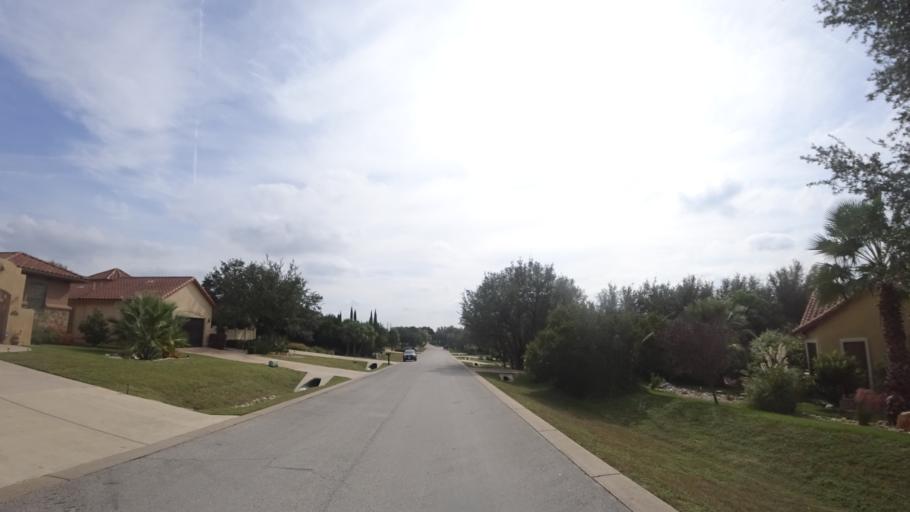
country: US
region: Texas
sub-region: Travis County
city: Hudson Bend
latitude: 30.3881
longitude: -97.9307
